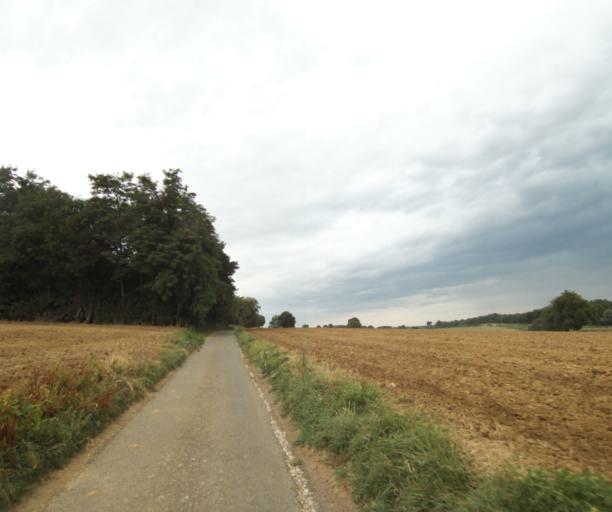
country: FR
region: Bourgogne
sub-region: Departement de Saone-et-Loire
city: Tournus
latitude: 46.5921
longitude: 4.9082
